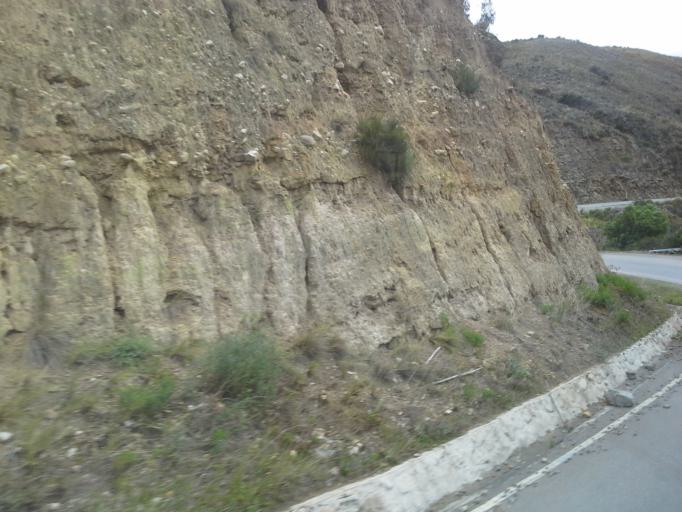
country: BO
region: Cochabamba
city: Colomi
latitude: -17.4015
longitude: -65.8149
